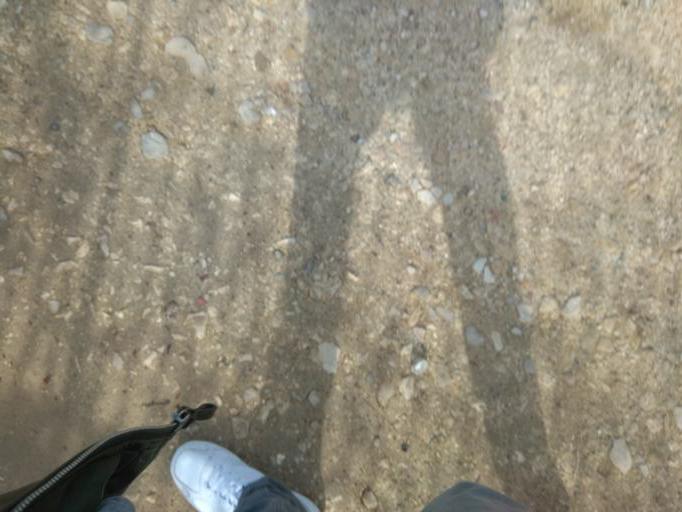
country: IT
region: Apulia
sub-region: Provincia di Bari
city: Bari
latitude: 41.1114
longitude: 16.9023
